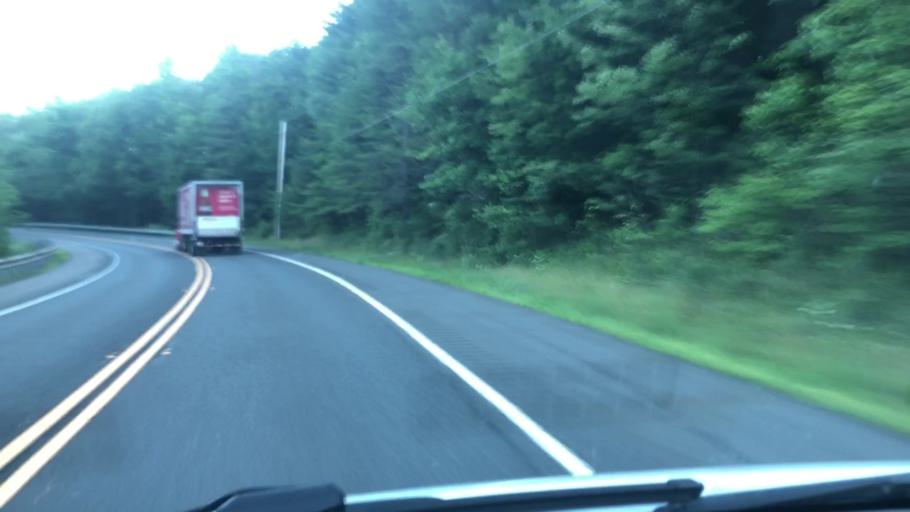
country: US
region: Massachusetts
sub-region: Hampshire County
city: Chesterfield
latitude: 42.4456
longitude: -72.8700
